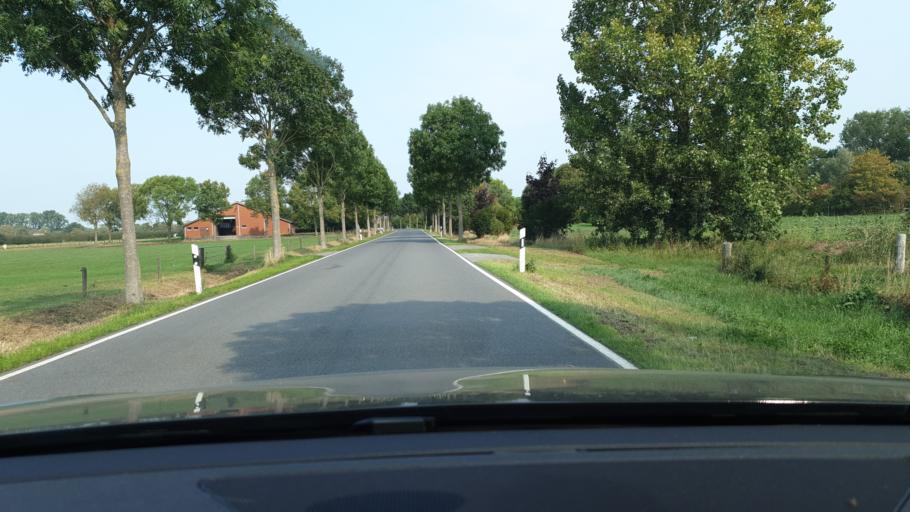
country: DE
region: North Rhine-Westphalia
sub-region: Regierungsbezirk Dusseldorf
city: Kranenburg
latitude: 51.8179
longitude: 6.0167
